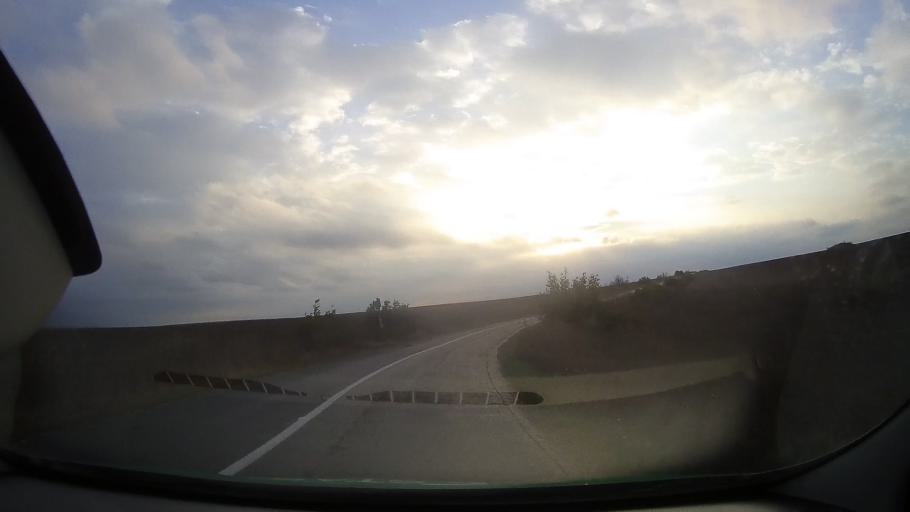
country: RO
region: Constanta
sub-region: Comuna Adamclisi
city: Adamclisi
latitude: 44.0182
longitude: 27.9054
